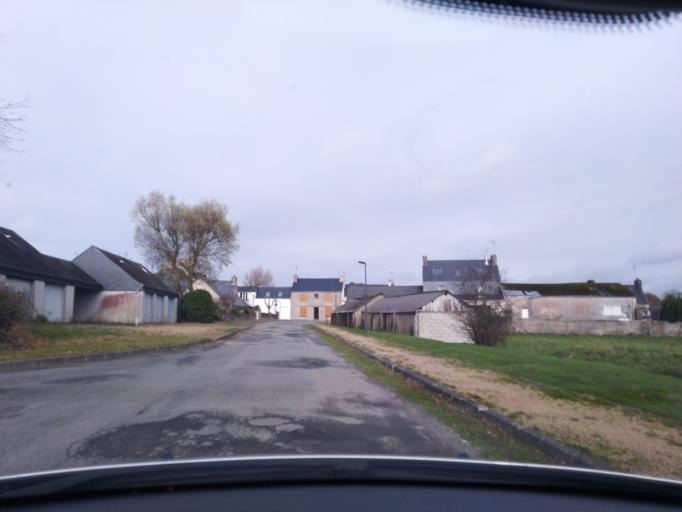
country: FR
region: Brittany
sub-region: Departement du Finistere
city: Guerlesquin
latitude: 48.5165
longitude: -3.5852
